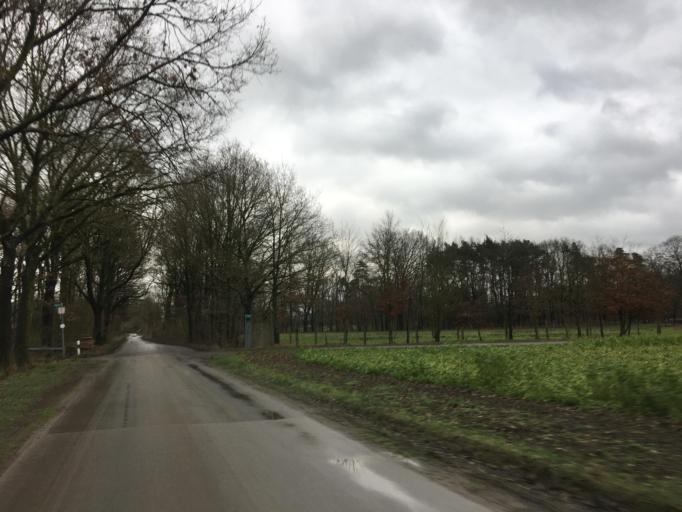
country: DE
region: North Rhine-Westphalia
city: Olfen
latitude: 51.7445
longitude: 7.3229
